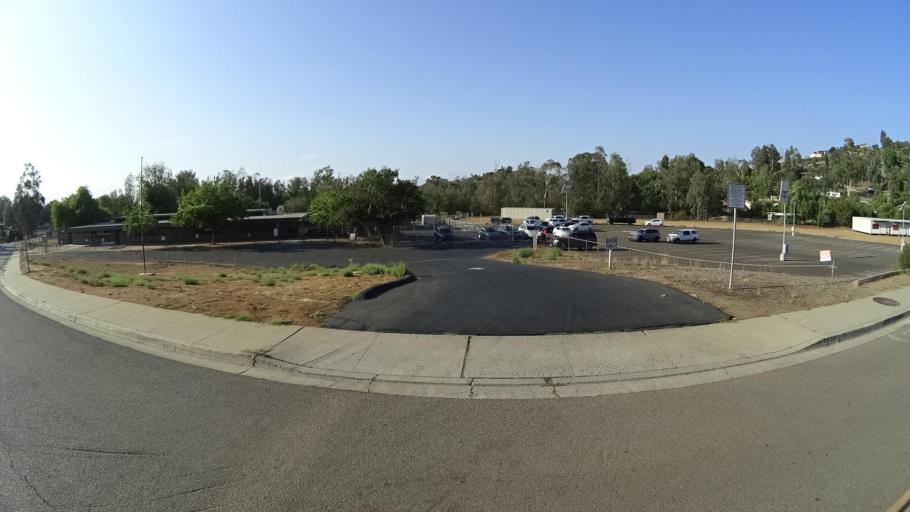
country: US
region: California
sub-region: San Diego County
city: Eucalyptus Hills
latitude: 32.8924
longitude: -116.9468
